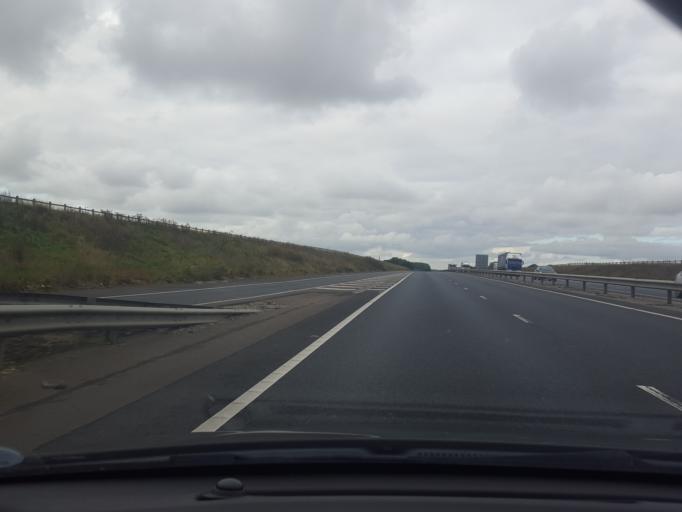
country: GB
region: England
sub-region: Suffolk
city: Stowmarket
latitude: 52.2072
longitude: 0.9718
